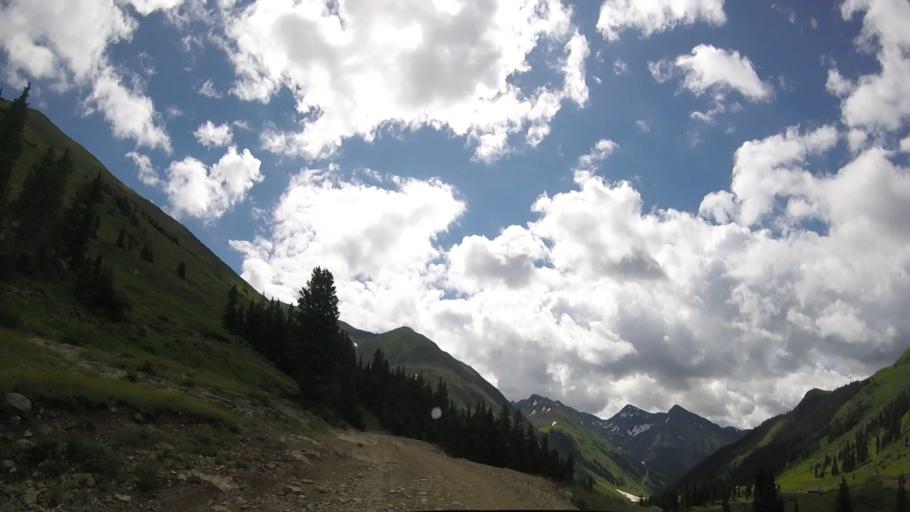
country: US
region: Colorado
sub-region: Ouray County
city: Ouray
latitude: 37.9321
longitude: -107.5696
